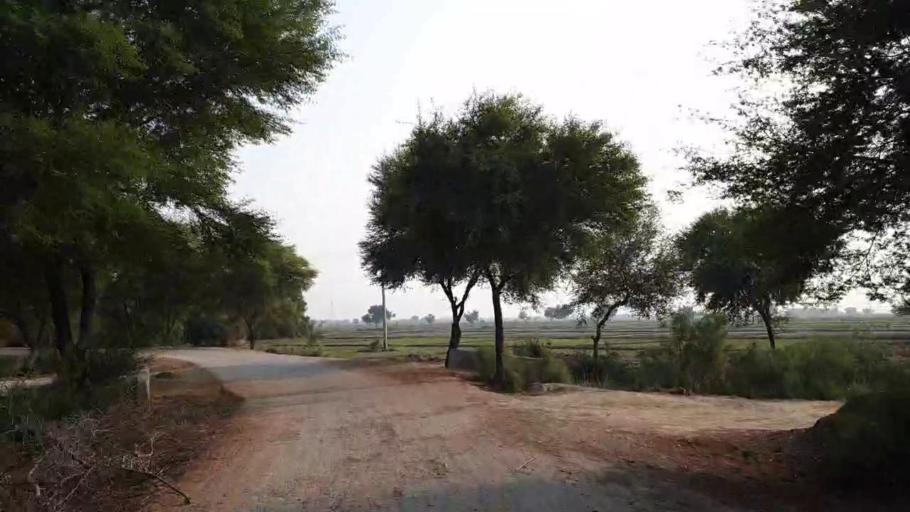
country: PK
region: Sindh
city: Bhan
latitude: 26.4999
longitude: 67.7635
